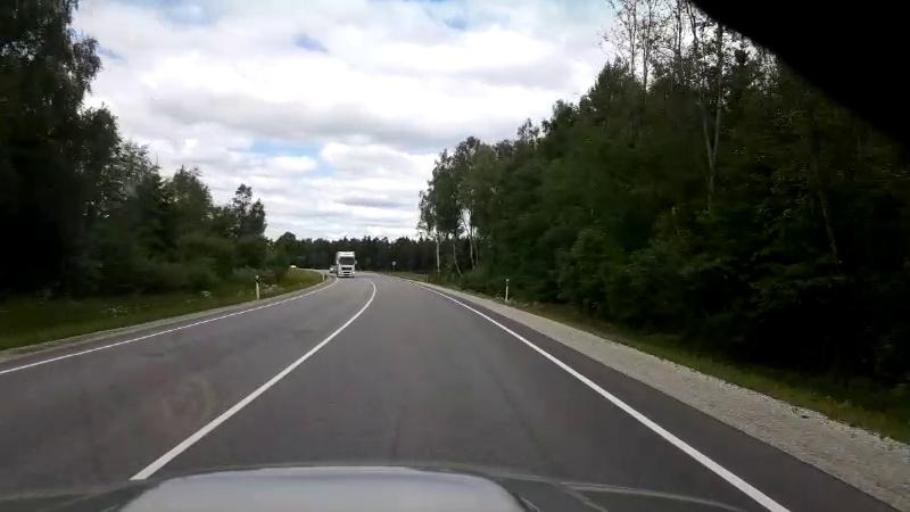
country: EE
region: Raplamaa
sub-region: Maerjamaa vald
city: Marjamaa
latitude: 58.9662
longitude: 24.4772
